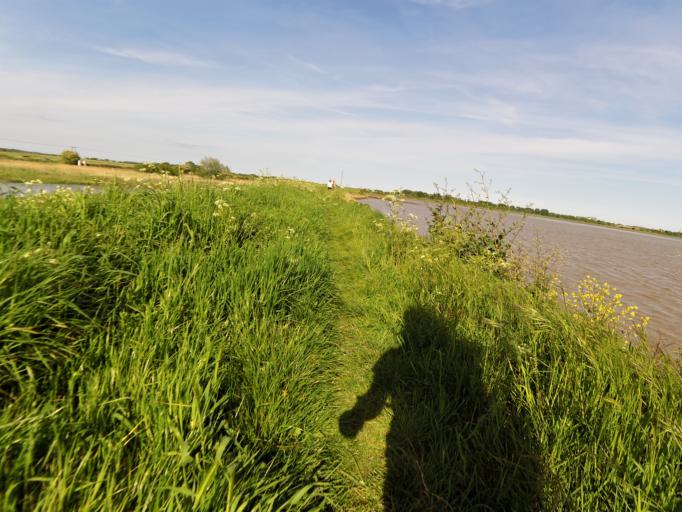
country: GB
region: England
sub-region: Norfolk
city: Great Yarmouth
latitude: 52.6186
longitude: 1.7026
